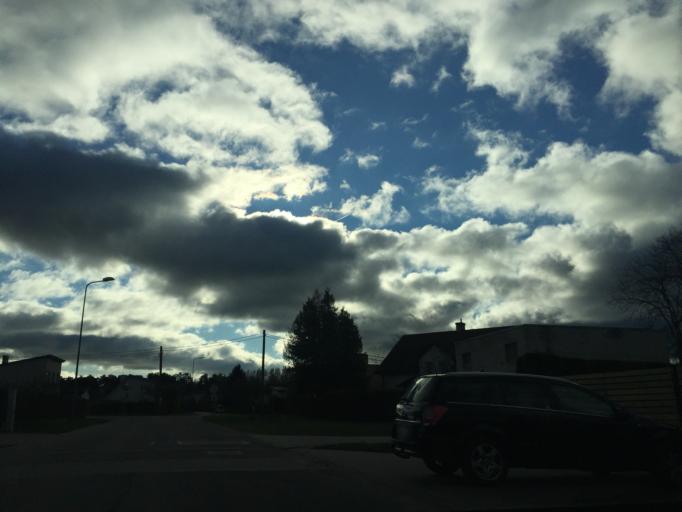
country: LV
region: Carnikava
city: Carnikava
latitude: 57.1292
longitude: 24.2666
